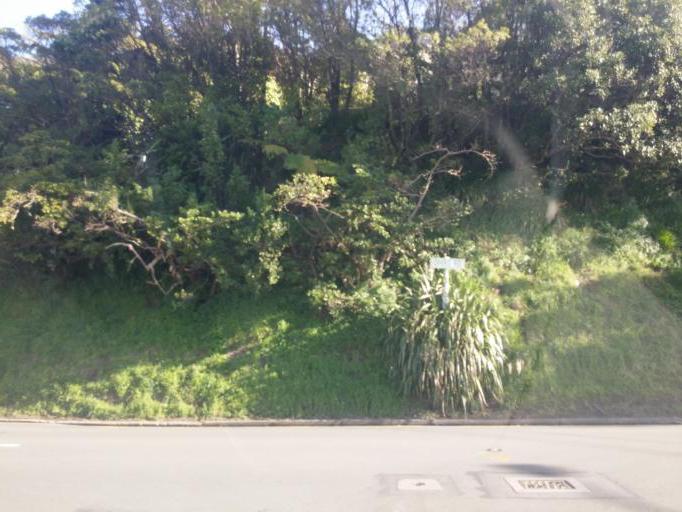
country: NZ
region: Wellington
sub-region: Wellington City
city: Brooklyn
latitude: -41.3065
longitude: 174.7632
